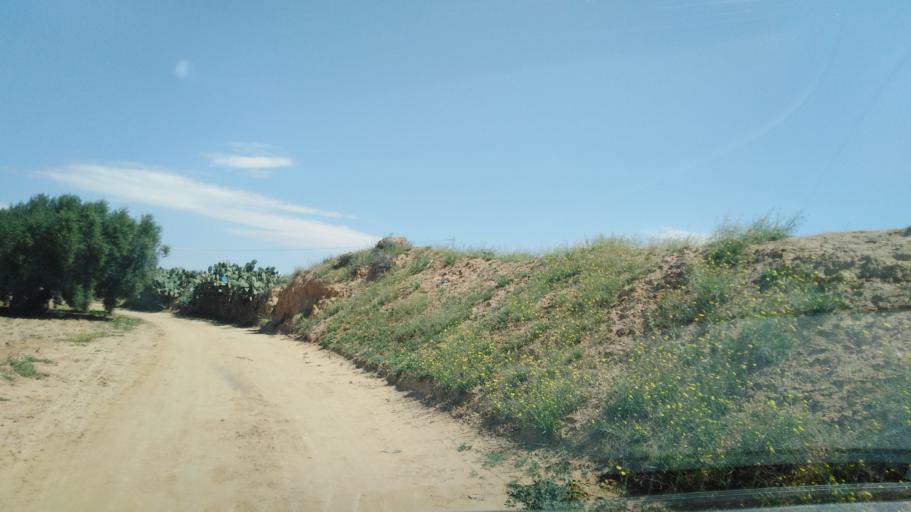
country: TN
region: Safaqis
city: Sfax
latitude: 34.7741
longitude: 10.5277
